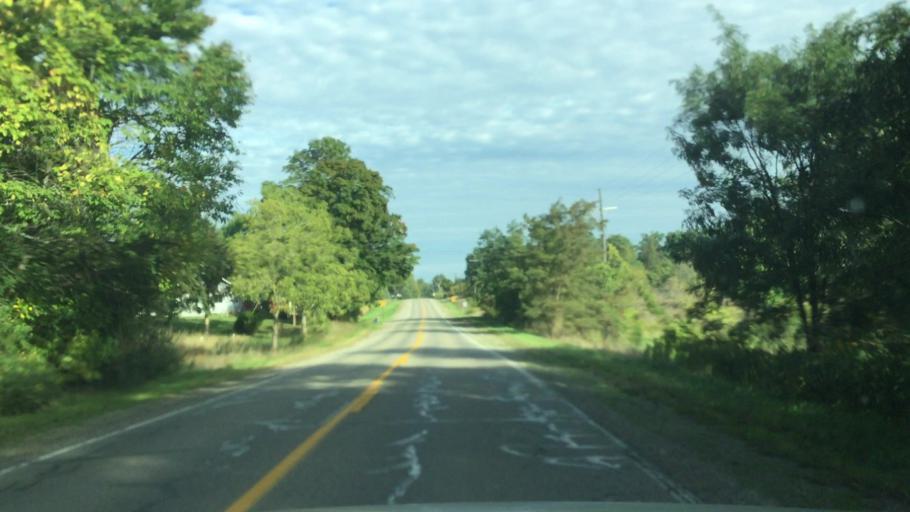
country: US
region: Michigan
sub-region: Livingston County
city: Howell
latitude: 42.5522
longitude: -83.8829
